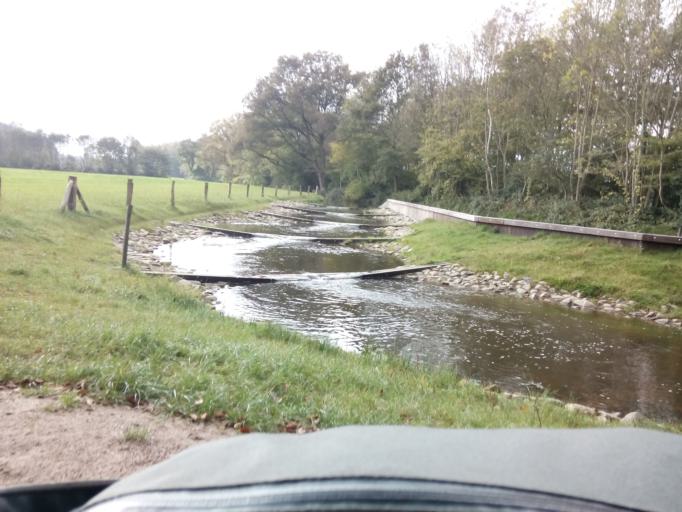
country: NL
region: Gelderland
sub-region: Gemeente Nijkerk
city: Nijkerk
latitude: 52.2467
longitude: 5.5358
